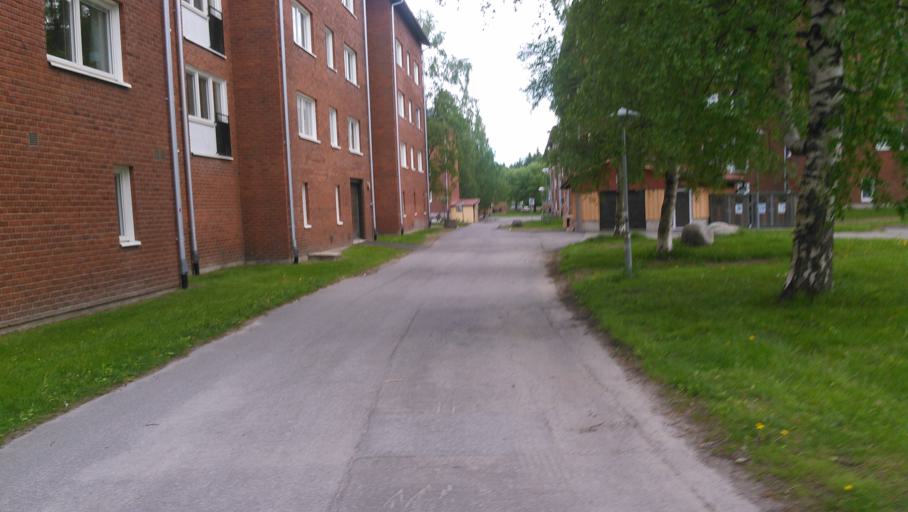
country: SE
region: Vaesterbotten
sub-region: Umea Kommun
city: Umea
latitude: 63.8077
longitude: 20.3128
